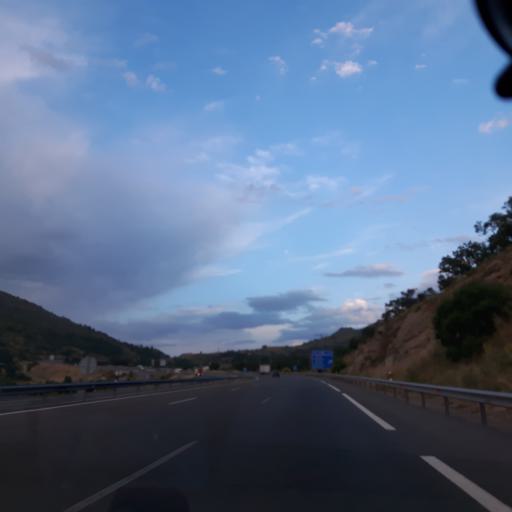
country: ES
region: Castille and Leon
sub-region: Provincia de Salamanca
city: Sorihuela
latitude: 40.4405
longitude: -5.6904
